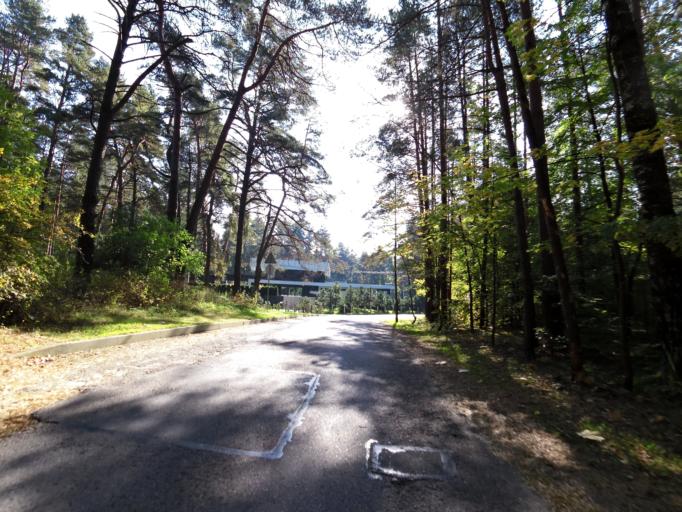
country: LT
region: Vilnius County
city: Rasos
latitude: 54.7310
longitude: 25.3127
